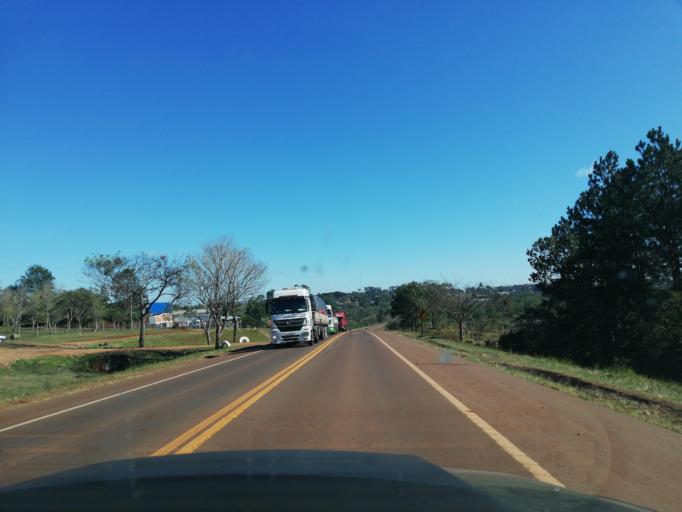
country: AR
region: Misiones
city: Aristobulo del Valle
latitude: -27.0964
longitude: -54.8725
